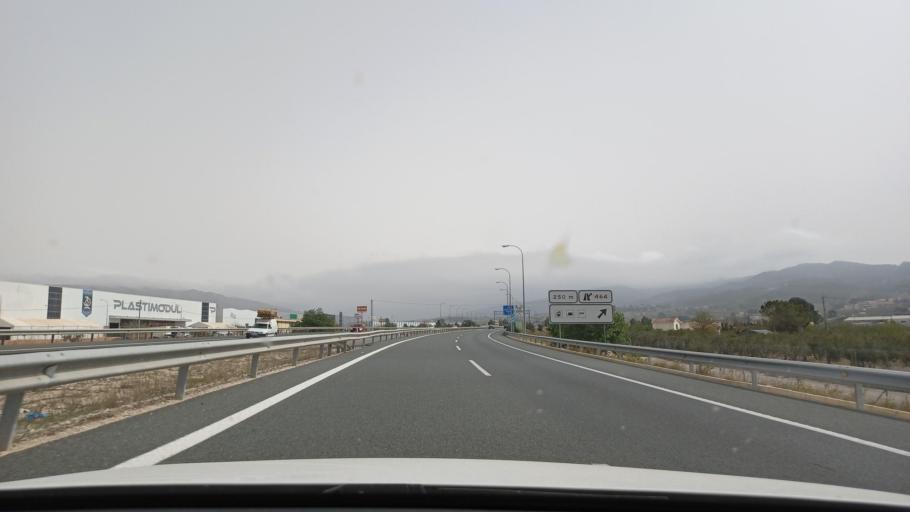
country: ES
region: Valencia
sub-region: Provincia de Alicante
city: Ibi
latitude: 38.6052
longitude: -0.5992
